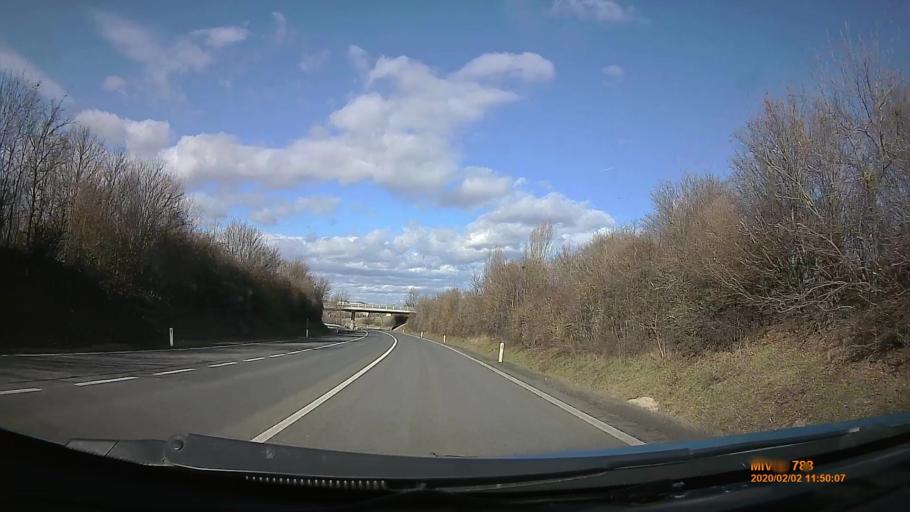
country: AT
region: Burgenland
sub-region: Eisenstadt-Umgebung
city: Klingenbach
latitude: 47.7593
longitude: 16.5436
